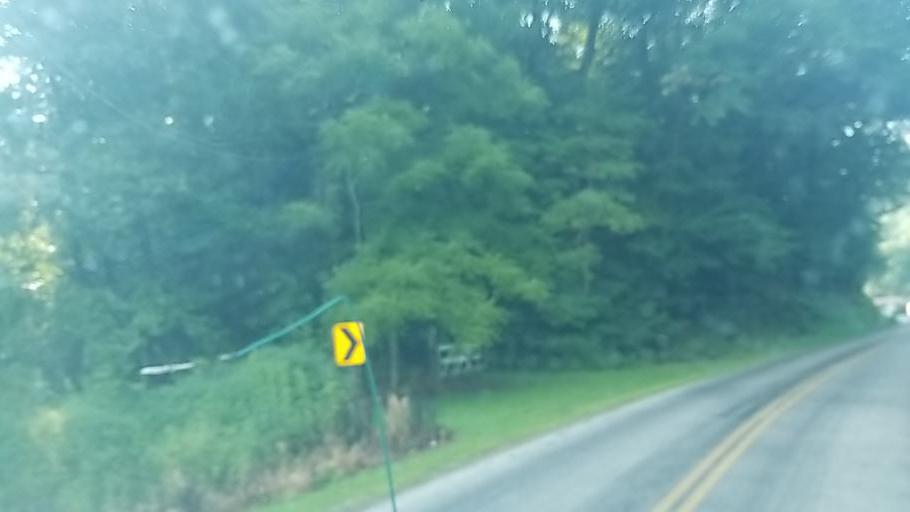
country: US
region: Ohio
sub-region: Wayne County
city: Wooster
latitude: 40.8673
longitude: -82.0168
